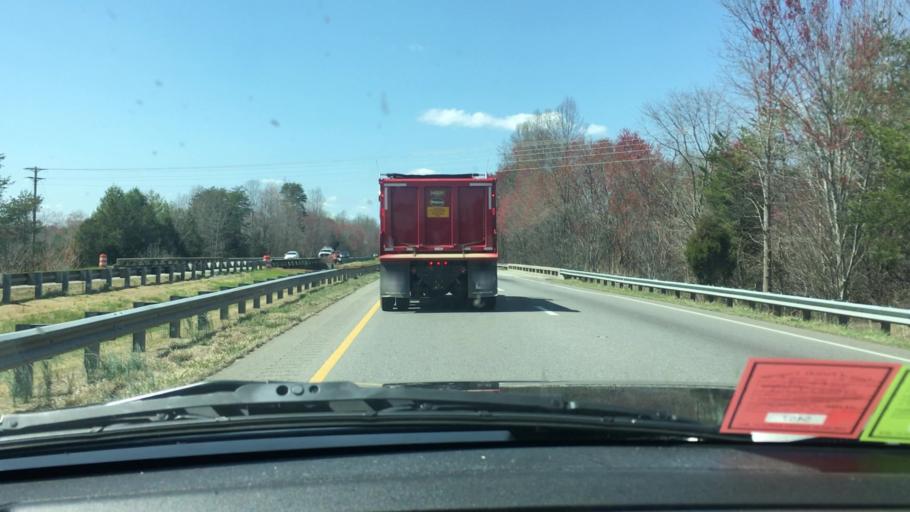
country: US
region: North Carolina
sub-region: Surry County
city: Pilot Mountain
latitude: 36.4289
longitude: -80.5241
